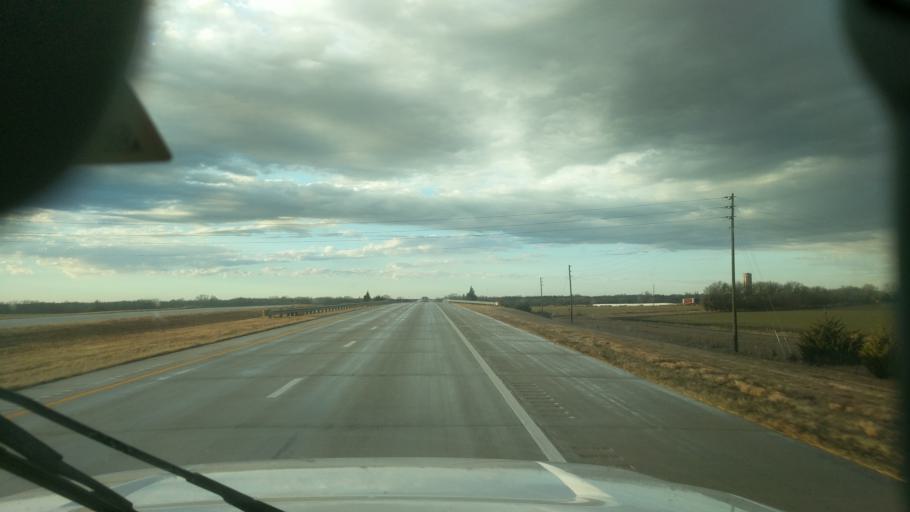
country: US
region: Kansas
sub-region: Harvey County
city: North Newton
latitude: 38.1009
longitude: -97.3704
